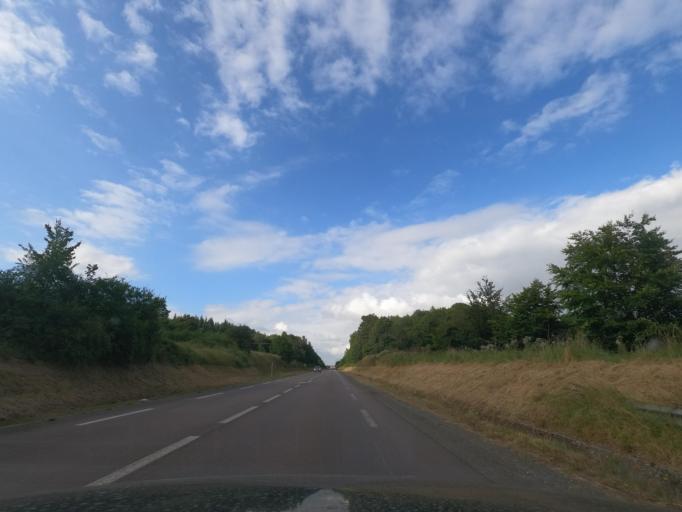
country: FR
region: Haute-Normandie
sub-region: Departement de l'Eure
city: Bernay
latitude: 49.0858
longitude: 0.5742
